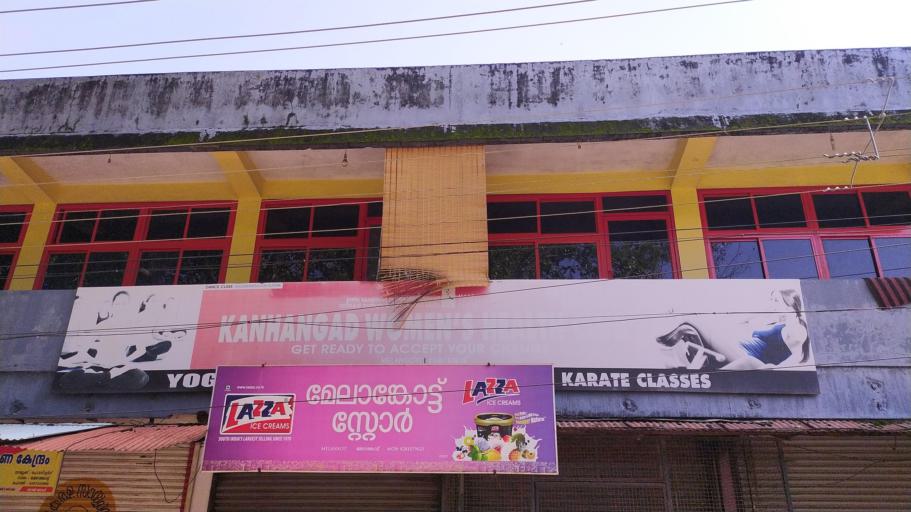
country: IN
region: Kerala
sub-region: Kasaragod District
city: Kannangad
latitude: 12.3246
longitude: 75.0931
